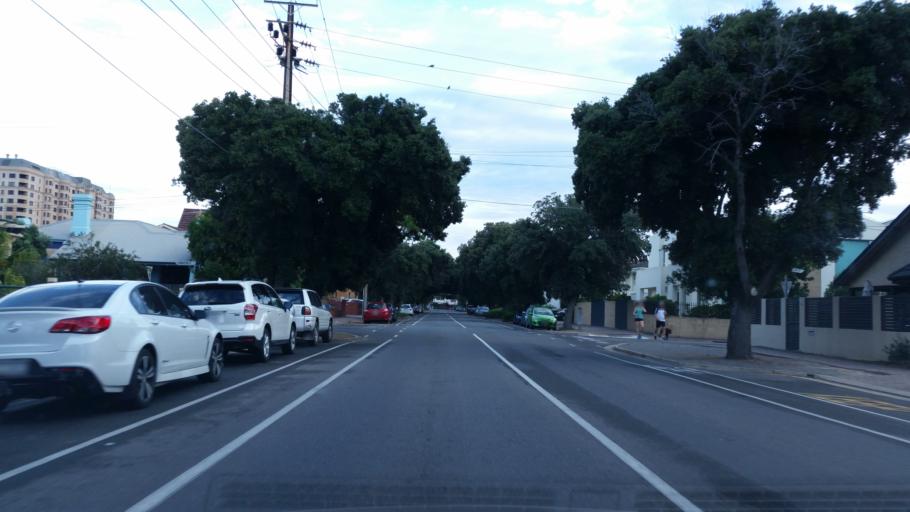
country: AU
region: South Australia
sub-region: Adelaide
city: Glenelg
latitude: -34.9836
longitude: 138.5133
